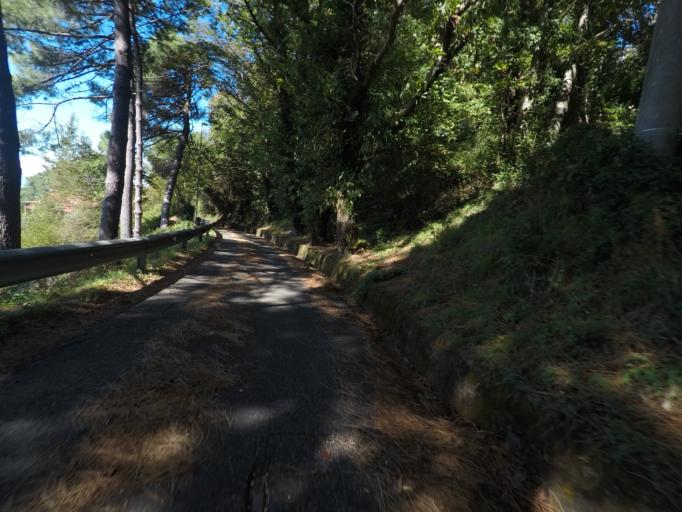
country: IT
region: Tuscany
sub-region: Provincia di Massa-Carrara
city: Montignoso
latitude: 44.0357
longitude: 10.1627
